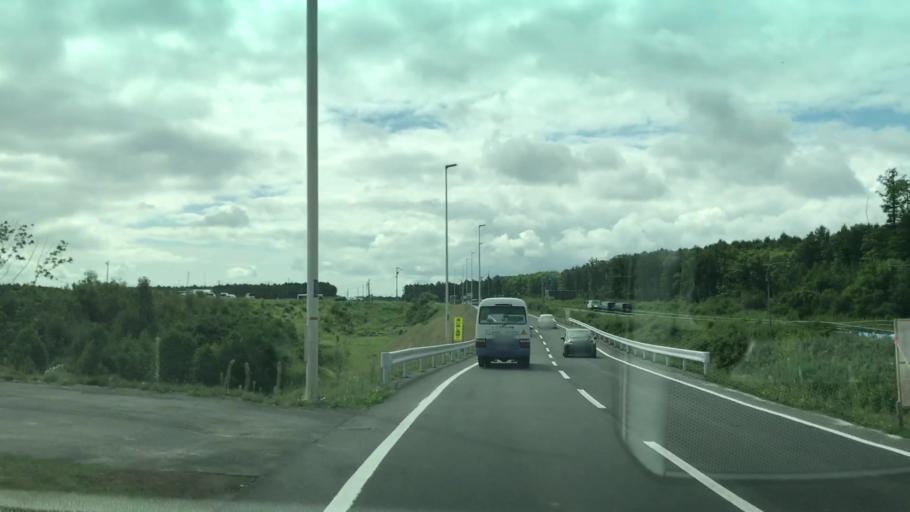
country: JP
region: Hokkaido
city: Chitose
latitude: 42.7748
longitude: 141.6792
